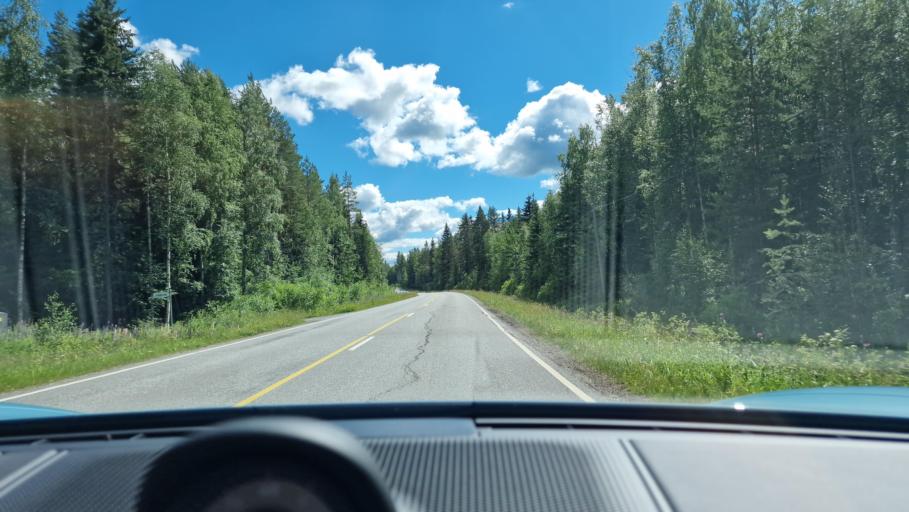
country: FI
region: Southern Ostrobothnia
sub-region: Jaerviseutu
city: Soini
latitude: 62.8278
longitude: 24.3414
